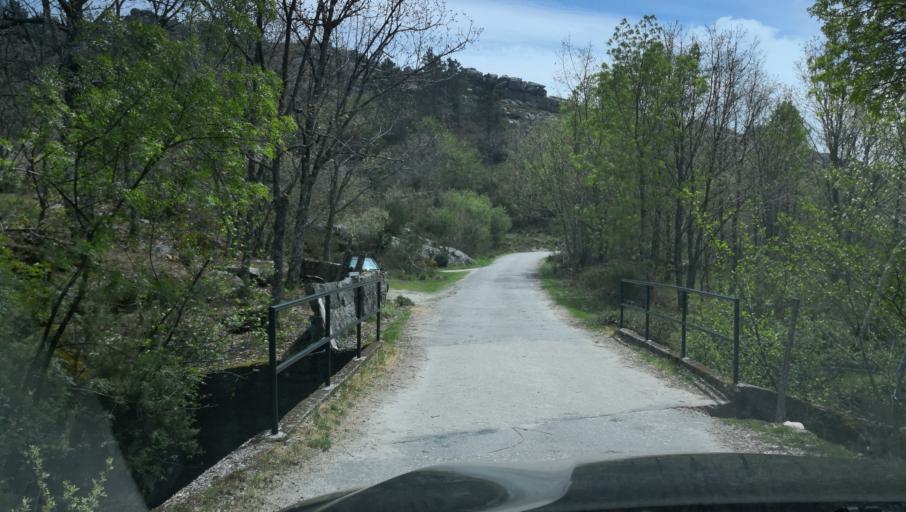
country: PT
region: Vila Real
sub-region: Vila Real
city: Vila Real
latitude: 41.3301
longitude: -7.8007
